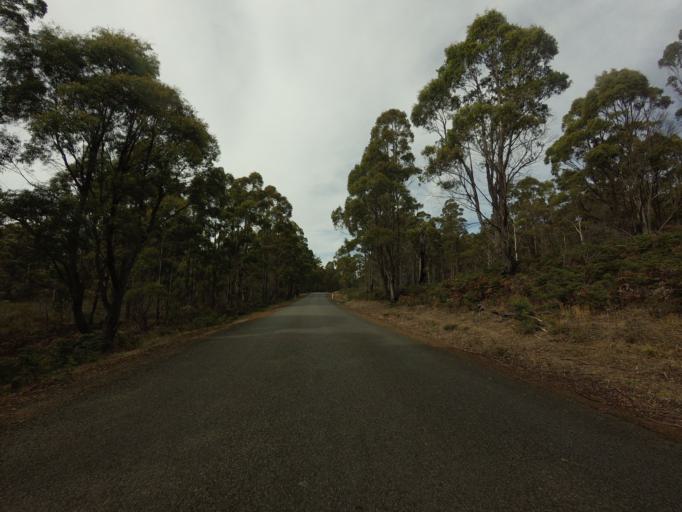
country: AU
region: Tasmania
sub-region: Sorell
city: Sorell
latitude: -42.5214
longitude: 147.6514
